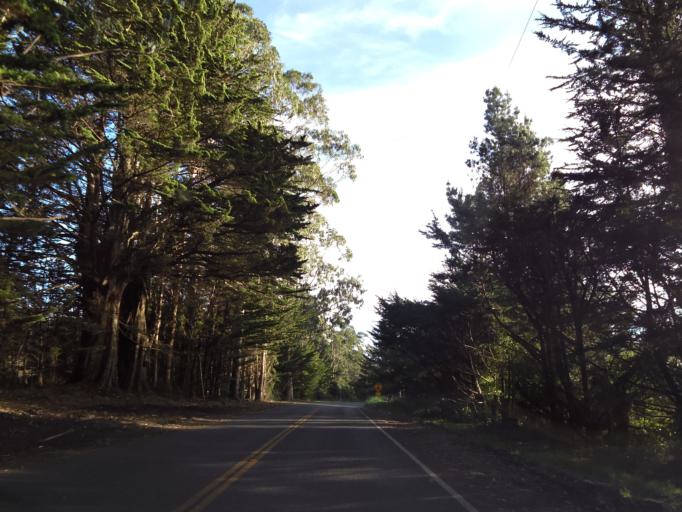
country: US
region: California
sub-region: Mendocino County
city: Fort Bragg
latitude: 39.3350
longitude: -123.8065
